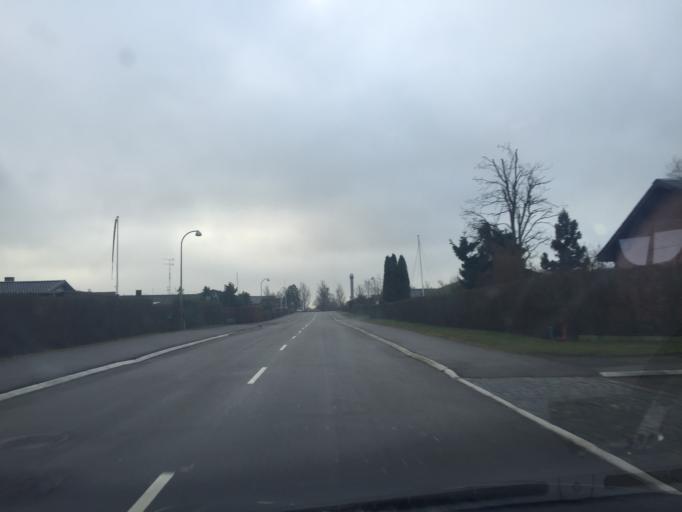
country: DK
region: Capital Region
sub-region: Hoje-Taastrup Kommune
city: Flong
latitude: 55.6821
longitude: 12.2390
